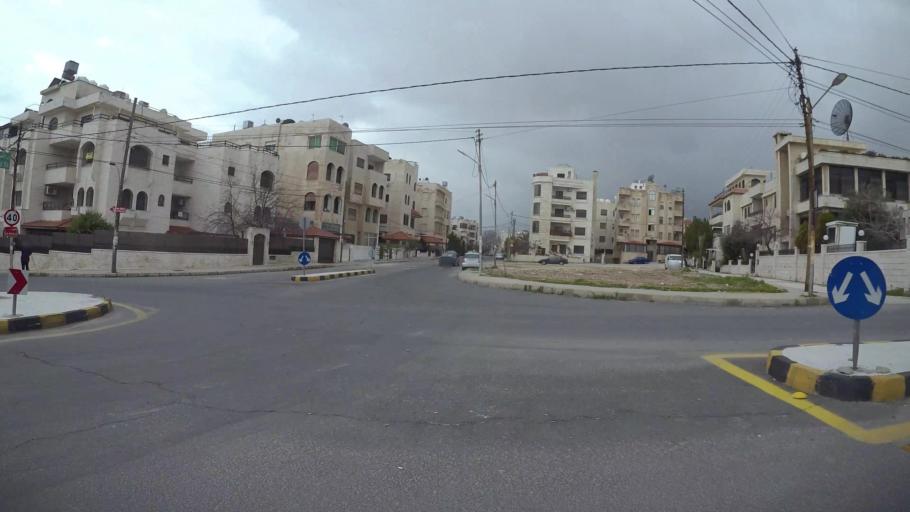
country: JO
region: Amman
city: Wadi as Sir
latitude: 31.9730
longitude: 35.8519
